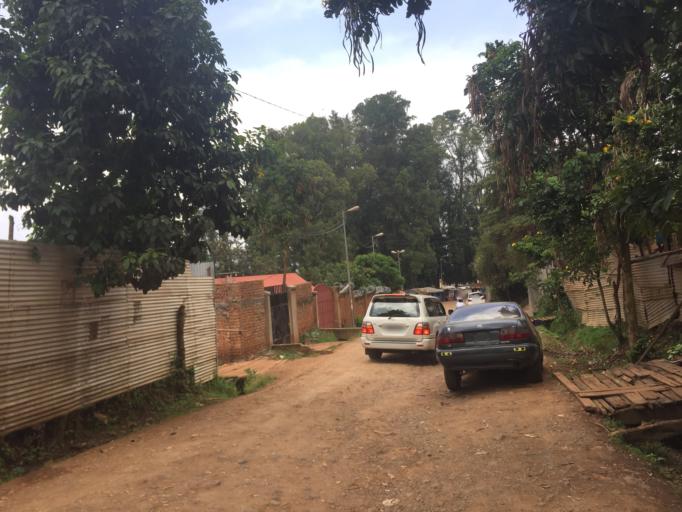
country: CD
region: South Kivu
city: Bukavu
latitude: -2.4852
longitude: 28.8589
